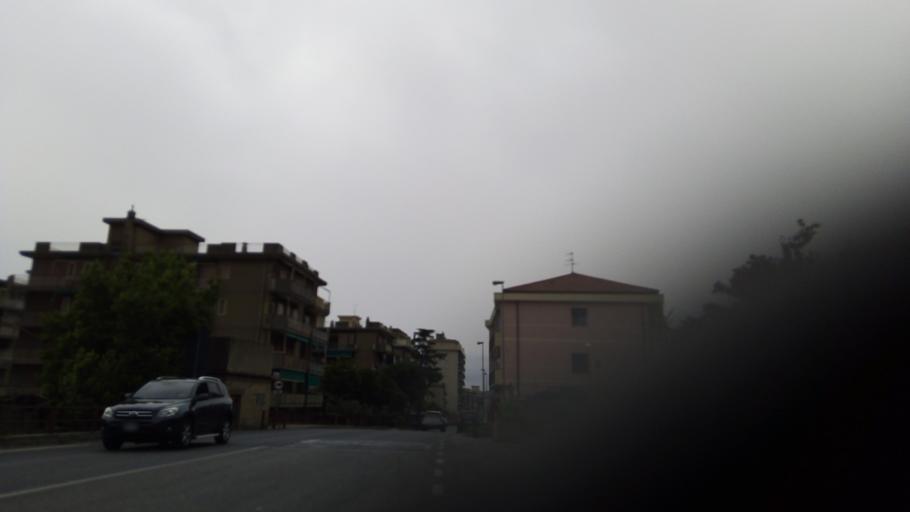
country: IT
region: Liguria
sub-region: Provincia di Savona
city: Borghetto Santo Spirito
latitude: 44.1138
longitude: 8.2321
